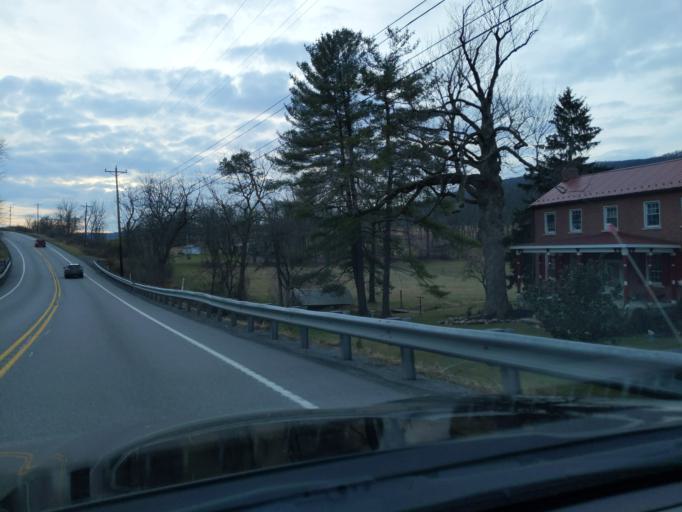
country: US
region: Pennsylvania
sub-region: Blair County
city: Williamsburg
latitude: 40.5348
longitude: -78.1919
